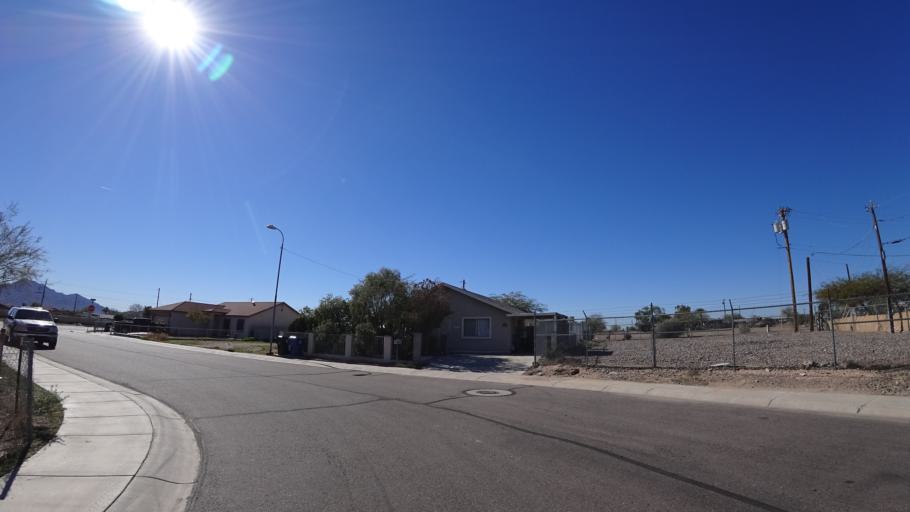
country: US
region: Arizona
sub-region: Maricopa County
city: Avondale
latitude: 33.4149
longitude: -112.3252
